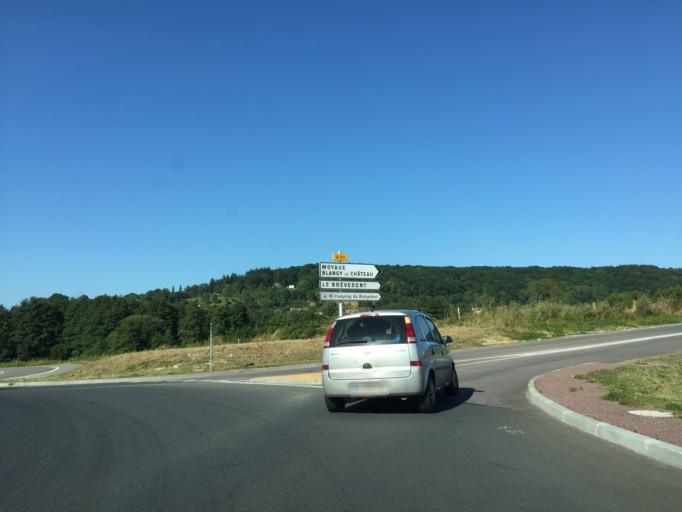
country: FR
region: Lower Normandy
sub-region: Departement du Calvados
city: Saint-Gatien-des-Bois
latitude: 49.2517
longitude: 0.2205
